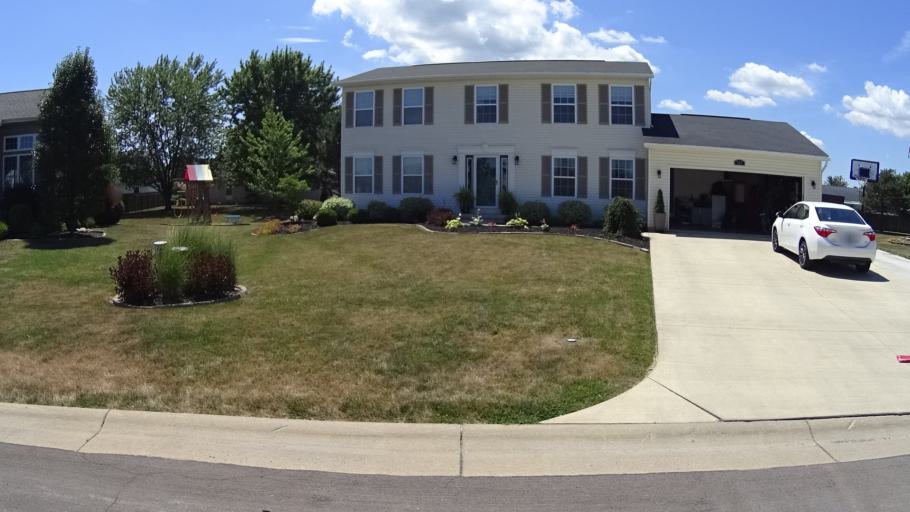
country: US
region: Ohio
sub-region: Erie County
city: Sandusky
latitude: 41.4023
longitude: -82.6945
